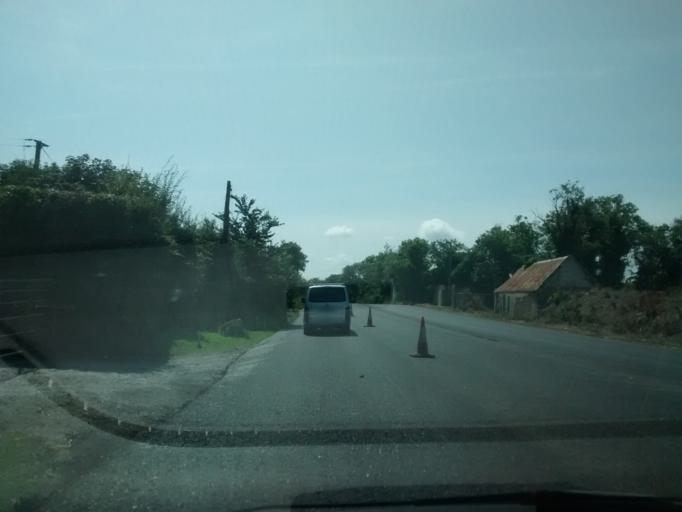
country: IE
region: Leinster
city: Lusk
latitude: 53.5142
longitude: -6.1917
